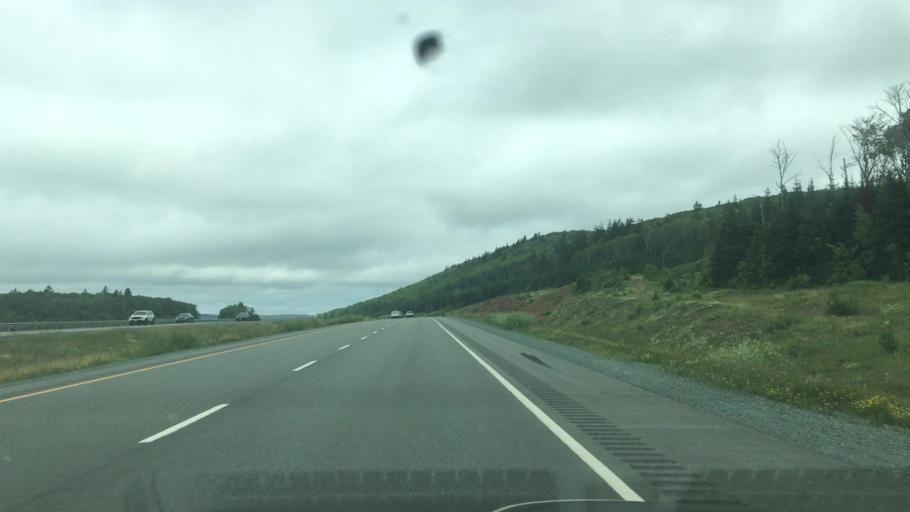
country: CA
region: Nova Scotia
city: Oxford
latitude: 45.5140
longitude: -63.6976
